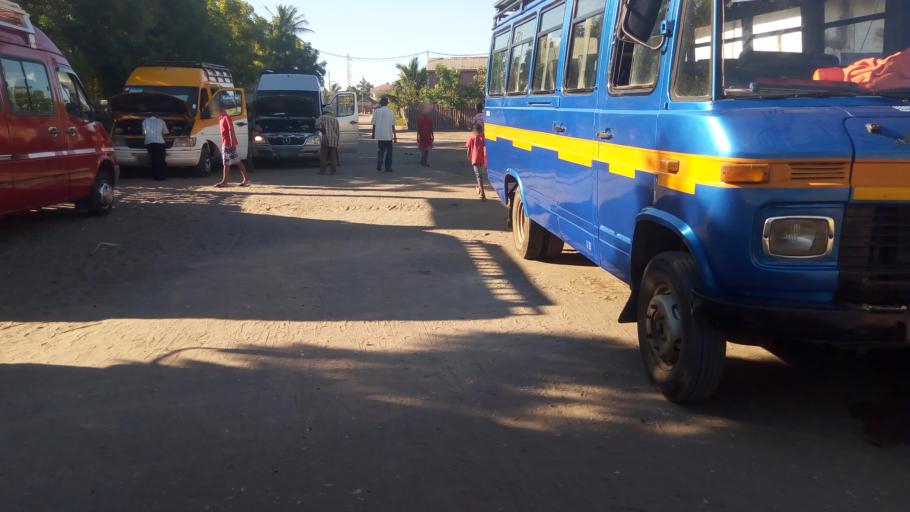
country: MG
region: Menabe
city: Morondava
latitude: -20.2957
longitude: 44.2815
